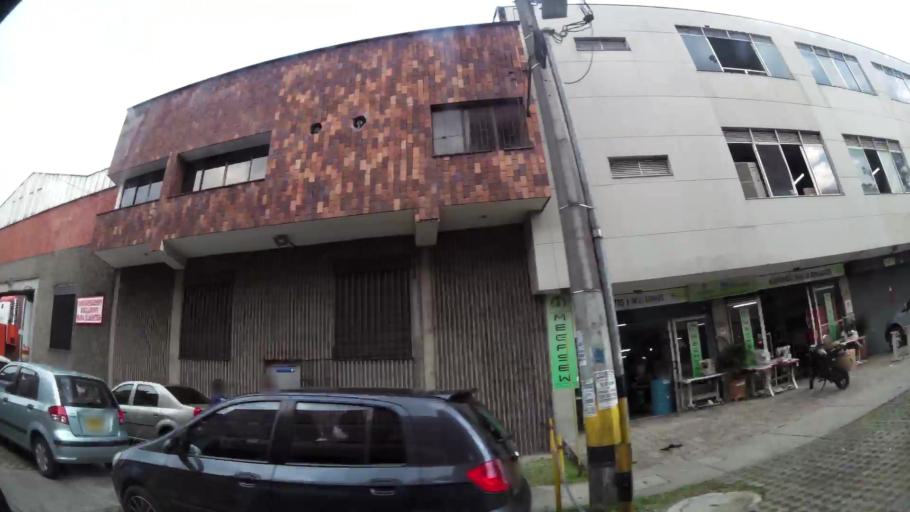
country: CO
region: Antioquia
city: Itagui
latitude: 6.1994
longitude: -75.5868
